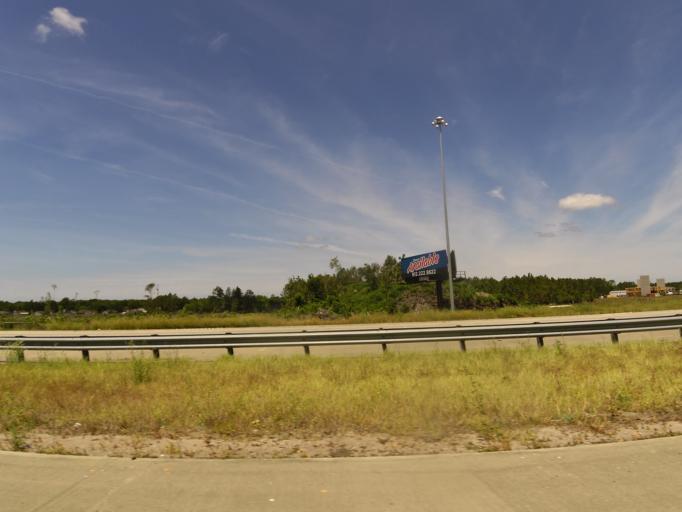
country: US
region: Georgia
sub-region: Glynn County
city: Dock Junction
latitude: 31.2388
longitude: -81.5054
